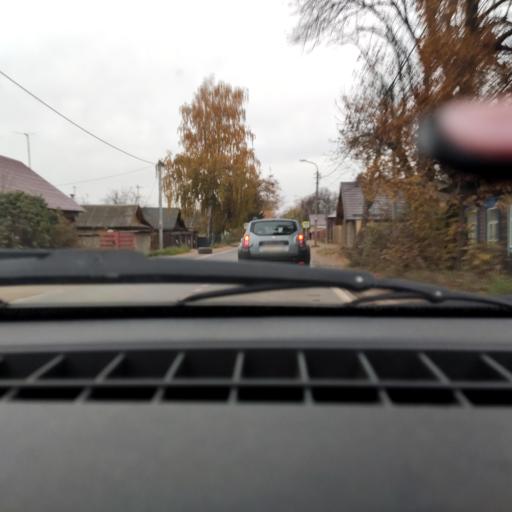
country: RU
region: Bashkortostan
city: Ufa
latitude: 54.8236
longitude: 56.1781
